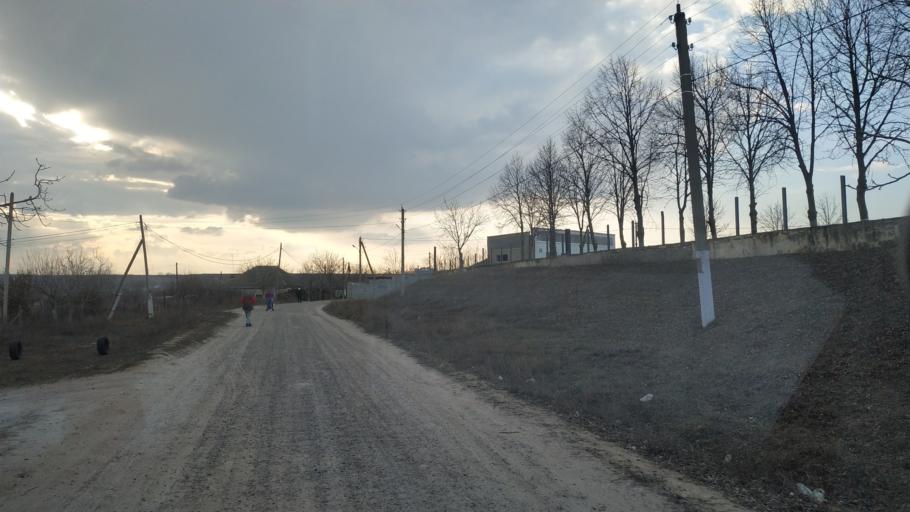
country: MD
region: Telenesti
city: Grigoriopol
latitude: 47.0091
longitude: 29.3042
